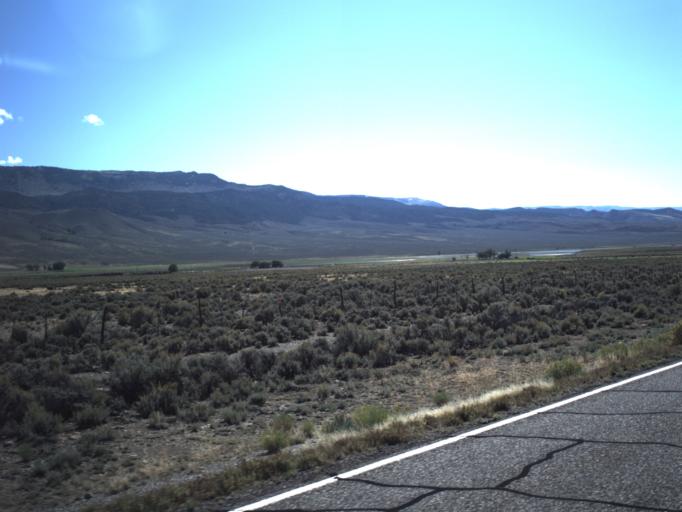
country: US
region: Utah
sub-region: Piute County
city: Junction
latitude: 38.2562
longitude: -111.9863
